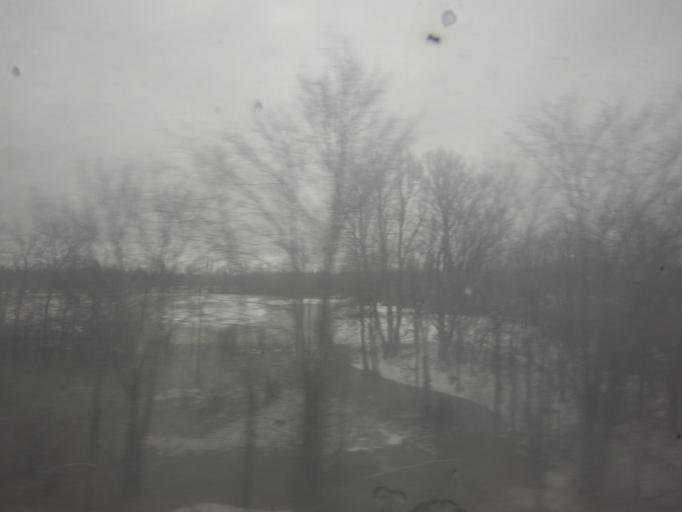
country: CA
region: Ontario
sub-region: Lanark County
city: Smiths Falls
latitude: 45.0343
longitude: -75.9298
